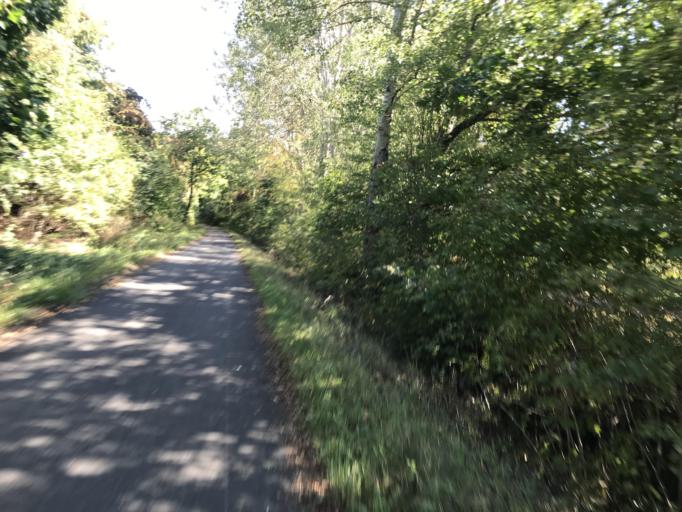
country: DE
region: Hesse
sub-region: Regierungsbezirk Kassel
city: Vohl
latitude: 51.2613
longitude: 8.9539
